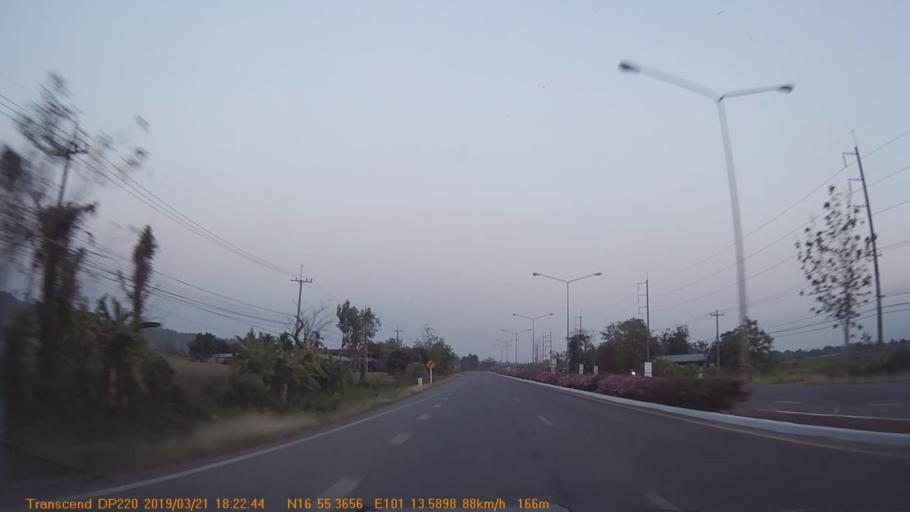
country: TH
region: Phetchabun
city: Lom Kao
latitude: 16.9225
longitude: 101.2266
